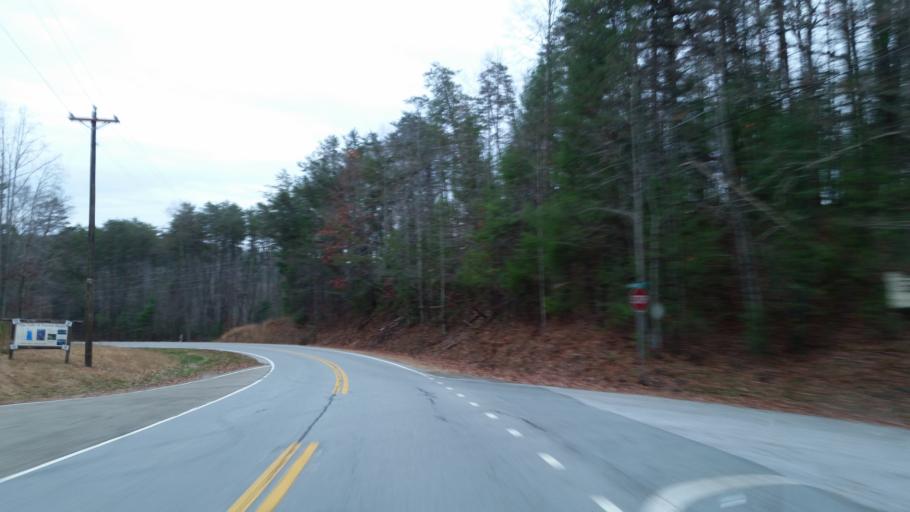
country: US
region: Georgia
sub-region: Pickens County
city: Jasper
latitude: 34.5296
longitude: -84.2834
